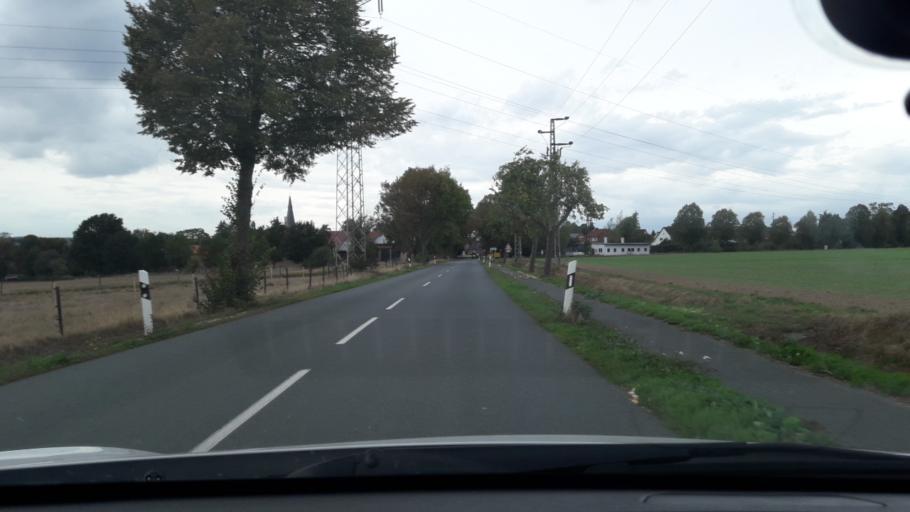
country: DE
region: Lower Saxony
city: Flothe
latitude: 52.0604
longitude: 10.4527
